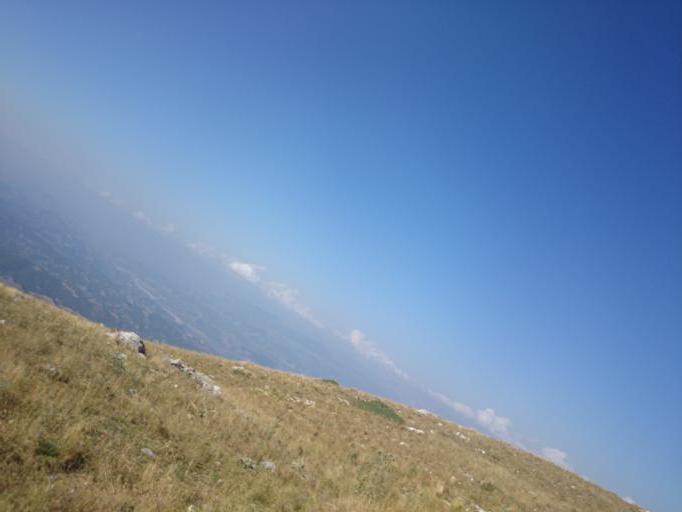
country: AL
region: Elbasan
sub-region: Rrethi i Gramshit
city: Kushove
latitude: 40.7286
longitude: 20.1462
